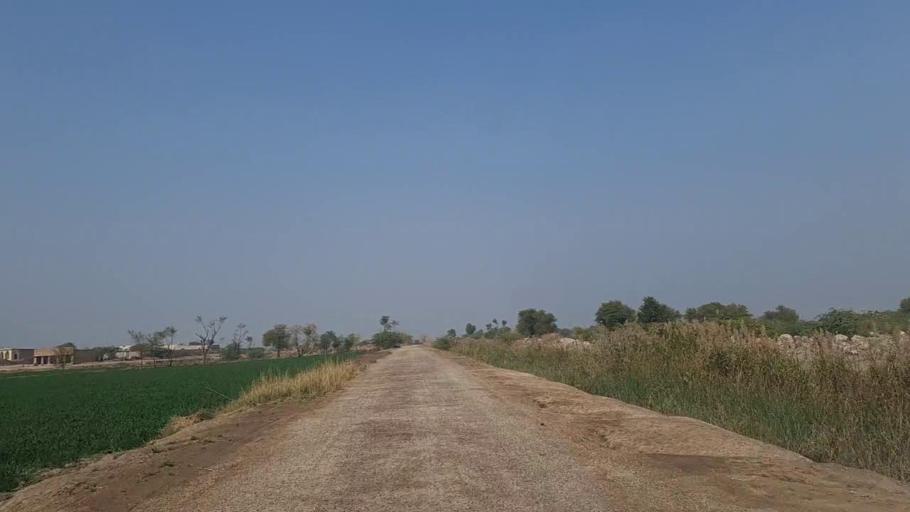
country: PK
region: Sindh
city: Nawabshah
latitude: 26.3682
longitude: 68.4260
